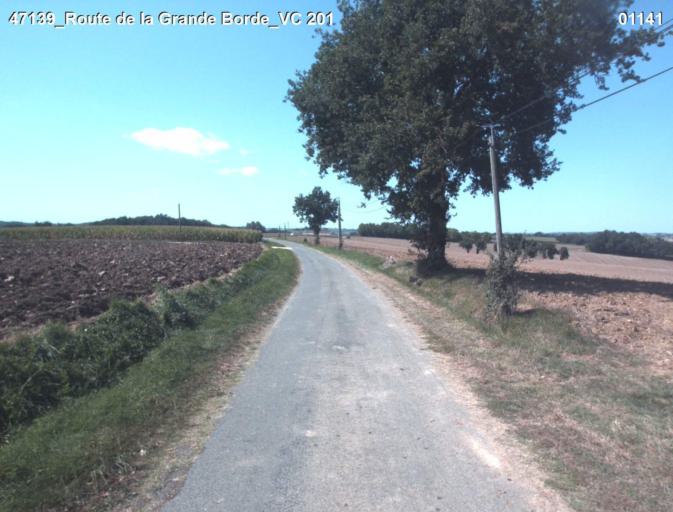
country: FR
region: Aquitaine
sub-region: Departement du Lot-et-Garonne
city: Nerac
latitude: 44.0710
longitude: 0.3887
